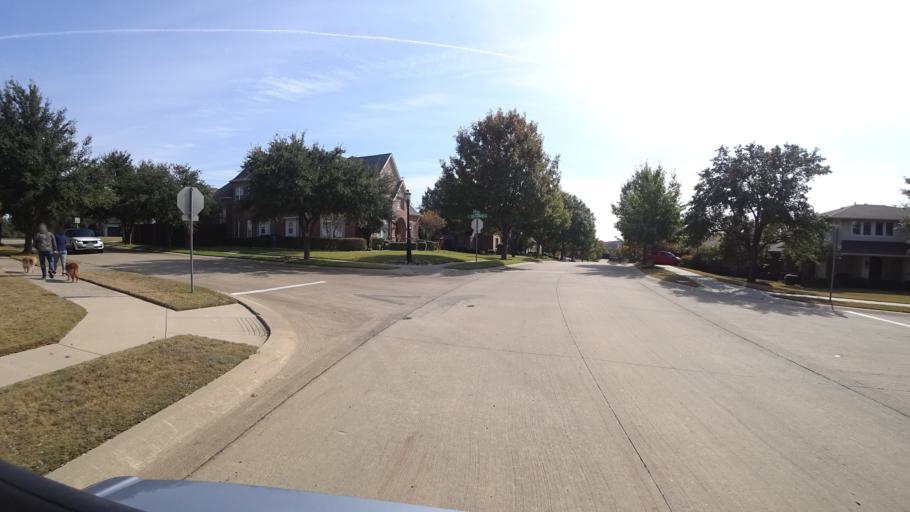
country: US
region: Texas
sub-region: Denton County
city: The Colony
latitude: 33.0381
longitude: -96.8953
